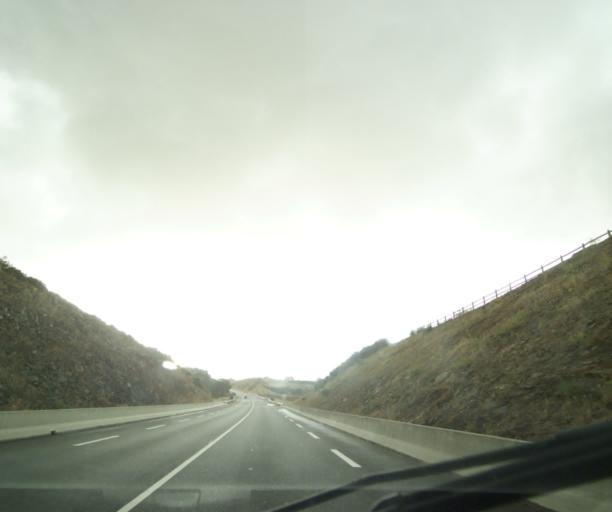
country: FR
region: Pays de la Loire
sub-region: Departement de la Vendee
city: Saint-Hilaire-de-Talmont
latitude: 46.4602
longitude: -1.6318
